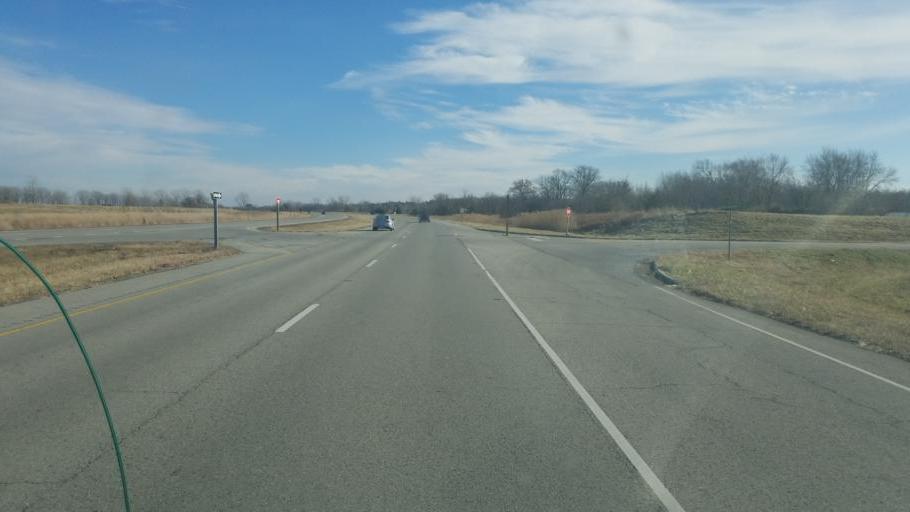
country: US
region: Illinois
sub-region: Williamson County
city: Marion
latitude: 37.7314
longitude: -88.7895
